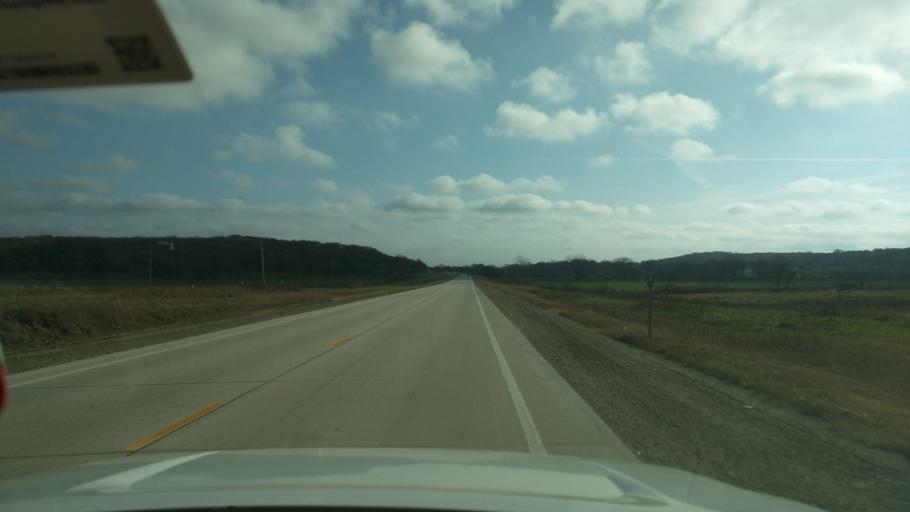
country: US
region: Kansas
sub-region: Montgomery County
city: Caney
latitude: 37.0685
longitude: -96.0298
